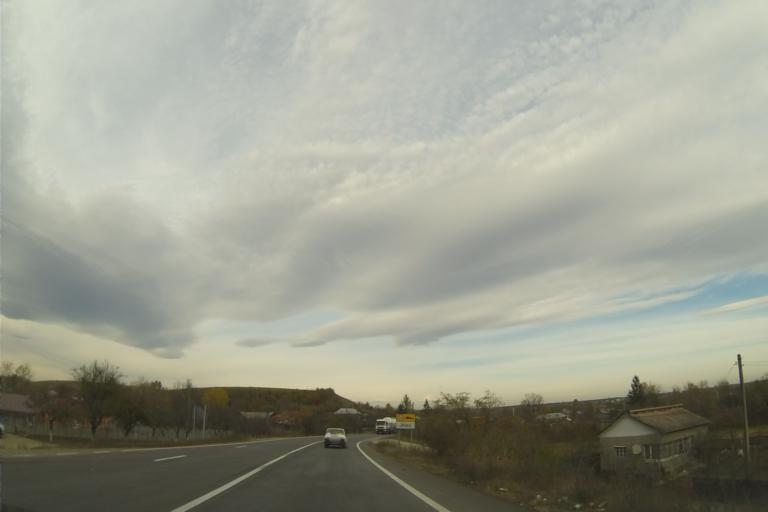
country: RO
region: Olt
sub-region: Comuna Scornicesti
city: Margineni Slobozia
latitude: 44.5404
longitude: 24.5384
